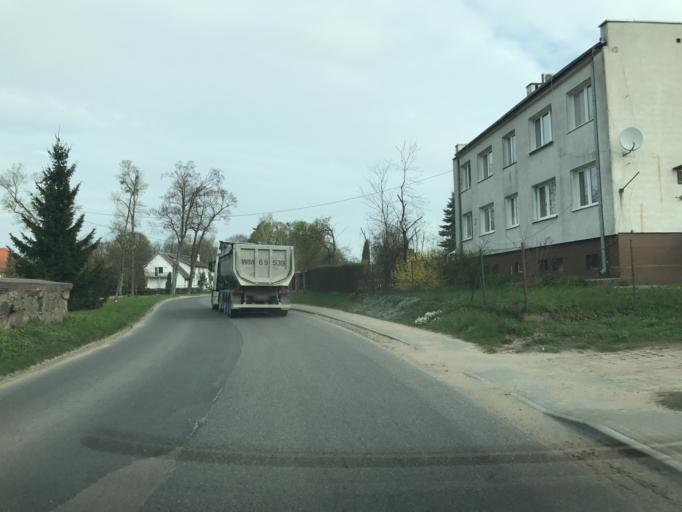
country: PL
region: Warmian-Masurian Voivodeship
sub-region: Powiat ostrodzki
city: Gierzwald
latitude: 53.5425
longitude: 20.0890
